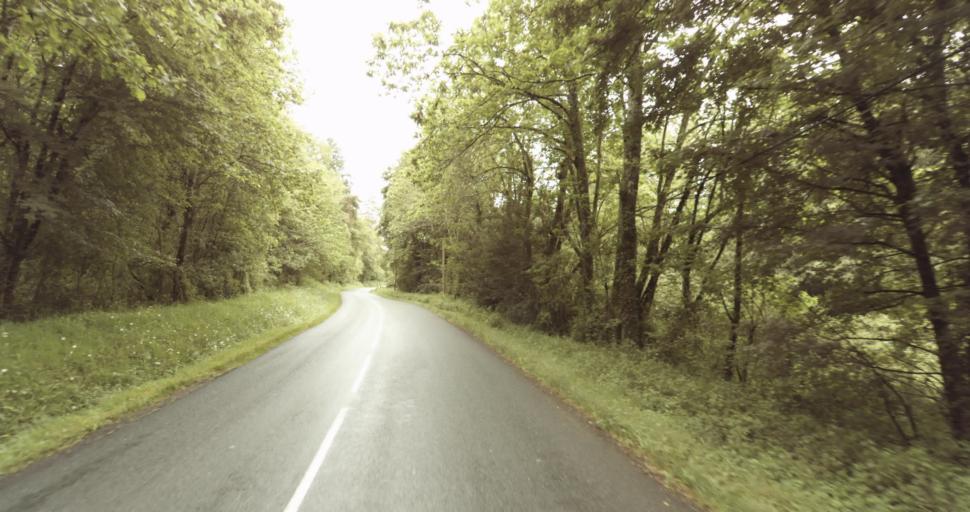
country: FR
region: Aquitaine
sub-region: Departement de la Dordogne
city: Belves
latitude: 44.7142
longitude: 0.9343
